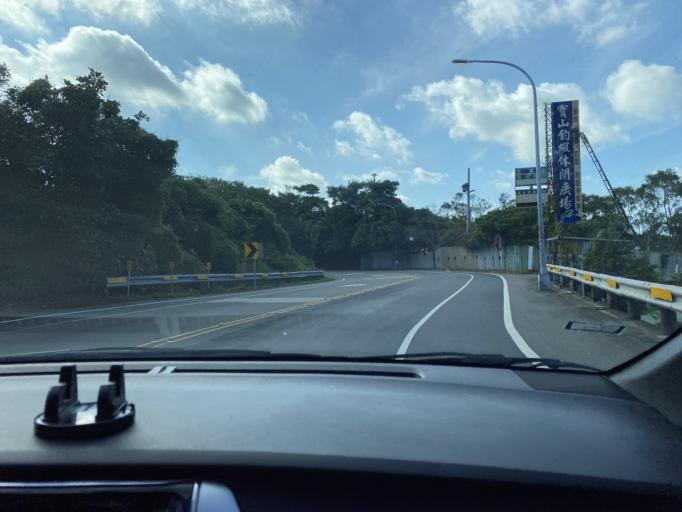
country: TW
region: Taiwan
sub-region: Changhua
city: Chang-hua
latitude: 24.0587
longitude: 120.5664
